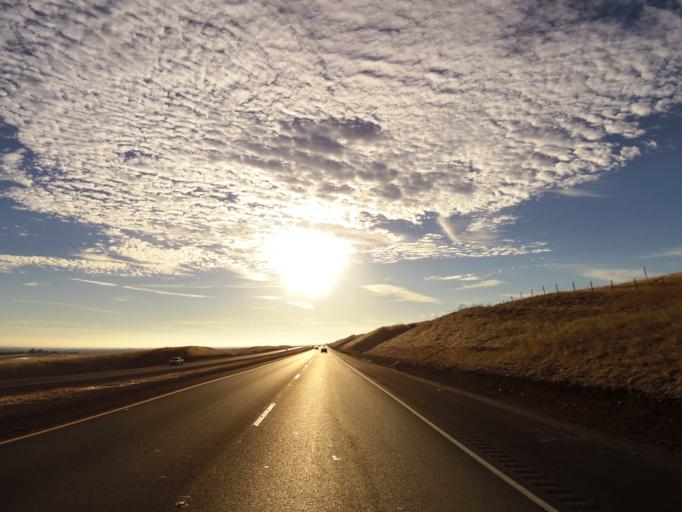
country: US
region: California
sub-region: San Joaquin County
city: Tracy
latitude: 37.6955
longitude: -121.4960
